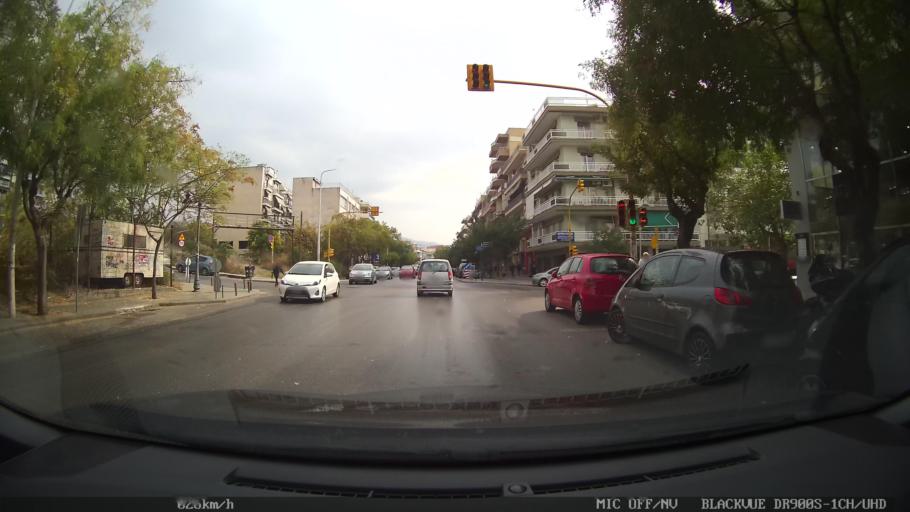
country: GR
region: Central Macedonia
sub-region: Nomos Thessalonikis
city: Triandria
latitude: 40.6116
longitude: 22.9855
